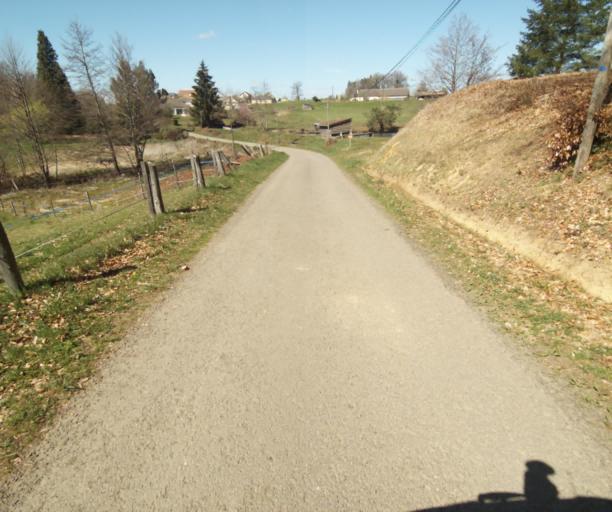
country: FR
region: Limousin
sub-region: Departement de la Correze
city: Saint-Mexant
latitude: 45.3025
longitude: 1.6708
